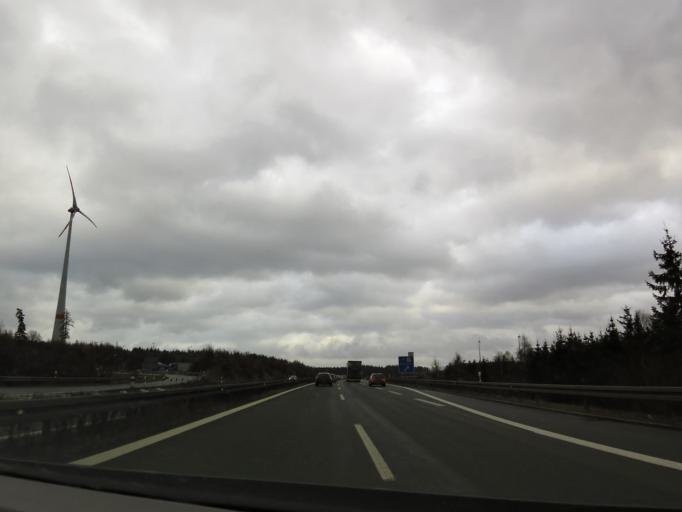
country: DE
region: Bavaria
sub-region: Upper Franconia
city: Gattendorf
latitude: 50.3268
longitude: 12.0226
